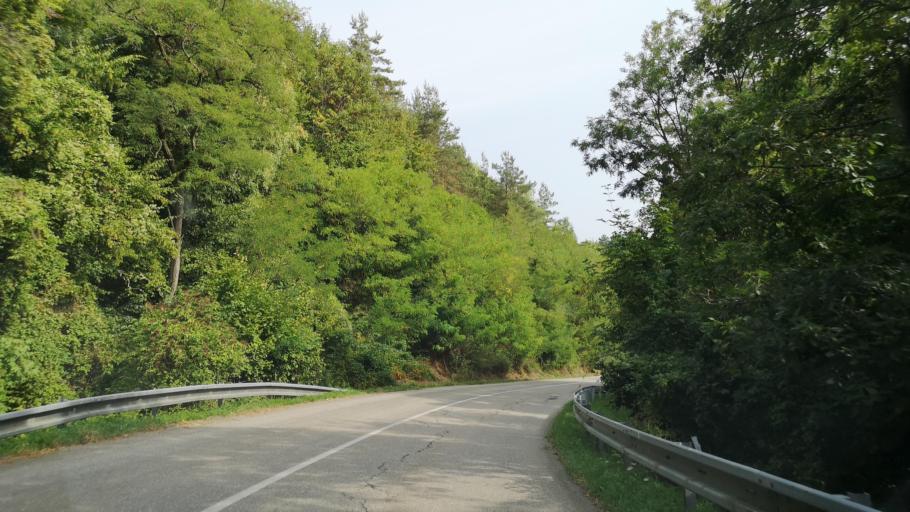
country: SK
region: Banskobystricky
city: Revuca
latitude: 48.5800
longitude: 20.0450
